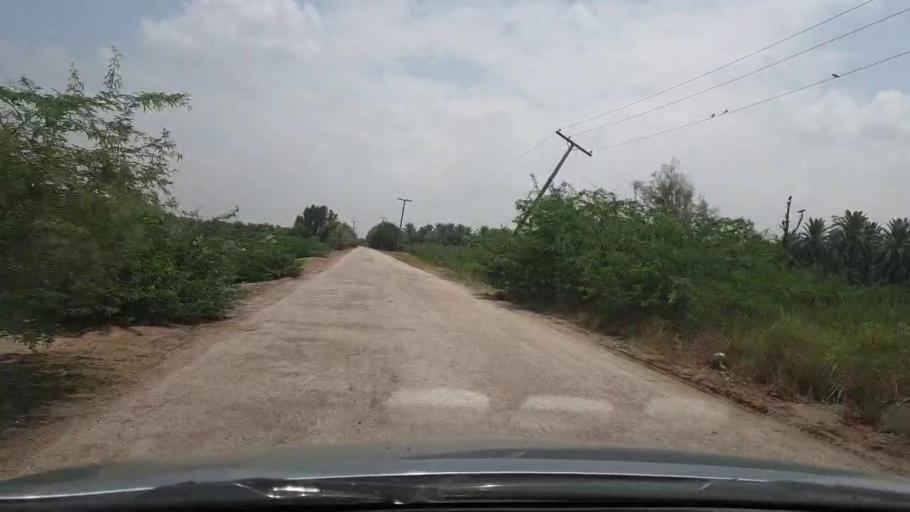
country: PK
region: Sindh
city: Khairpur
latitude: 27.4378
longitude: 68.7538
